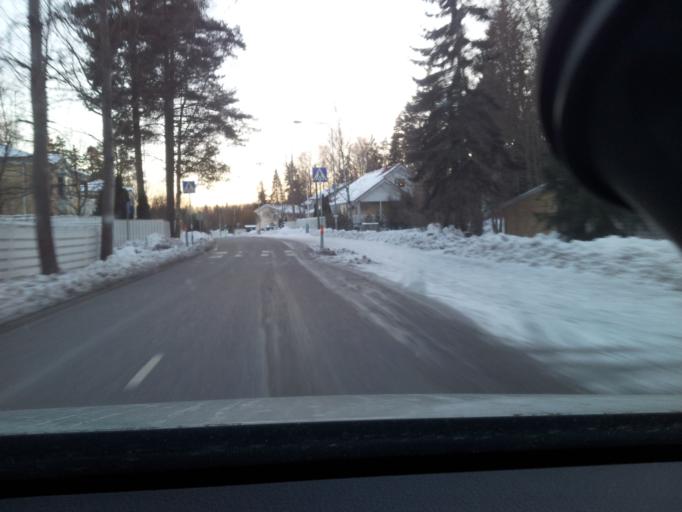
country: FI
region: Uusimaa
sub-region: Helsinki
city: Espoo
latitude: 60.1594
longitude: 24.6804
